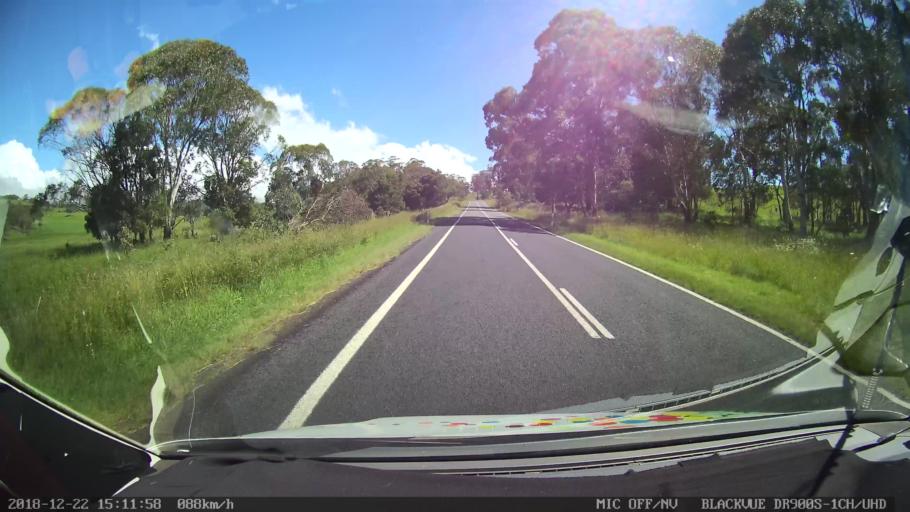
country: AU
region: New South Wales
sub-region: Bellingen
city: Dorrigo
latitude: -30.3499
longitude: 152.3977
